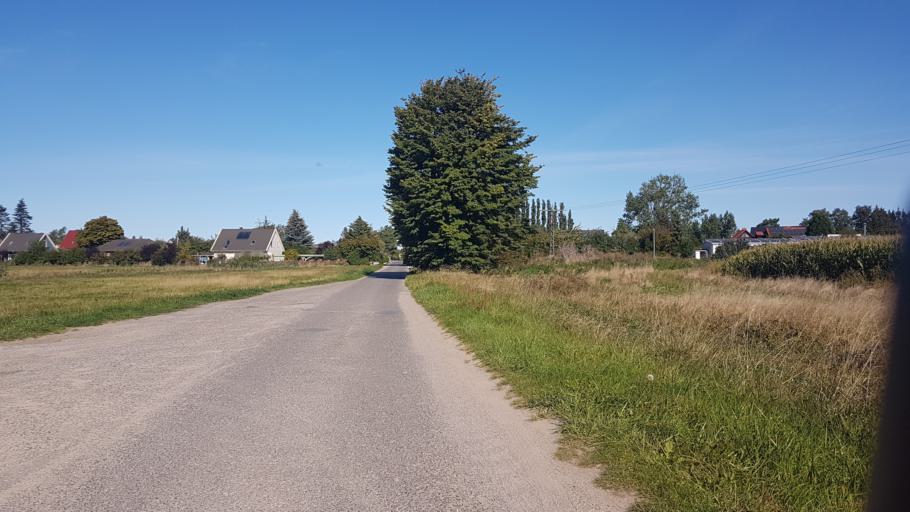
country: DE
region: Mecklenburg-Vorpommern
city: Sagard
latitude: 54.5415
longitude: 13.5089
